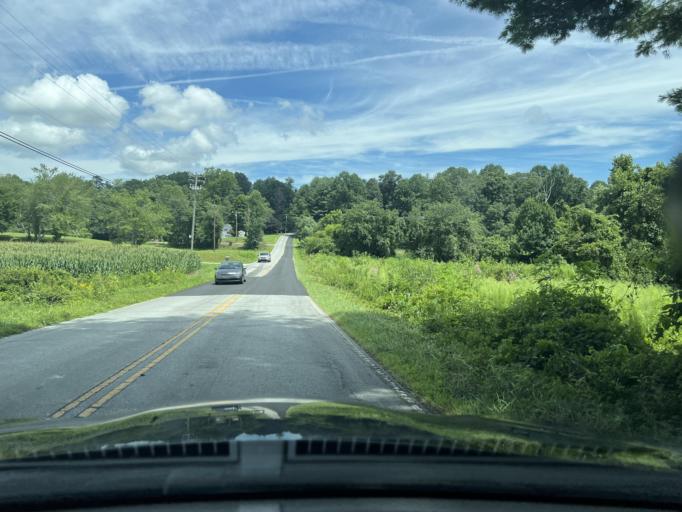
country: US
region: North Carolina
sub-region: Henderson County
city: Fruitland
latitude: 35.3940
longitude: -82.3863
